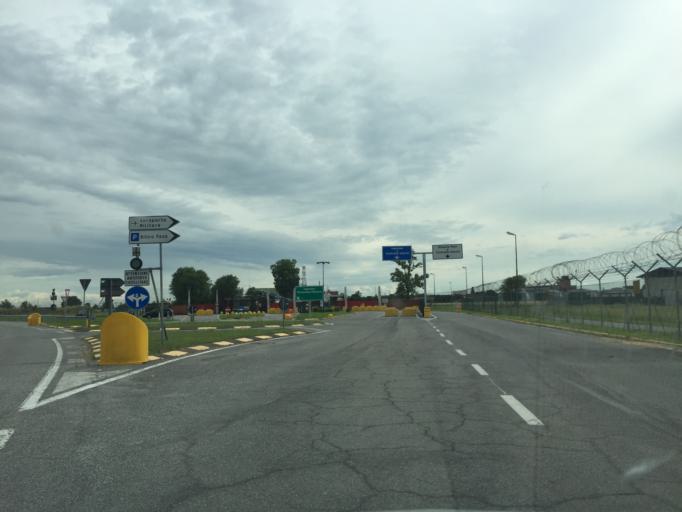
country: IT
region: Lombardy
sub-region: Provincia di Brescia
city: Ghedi
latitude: 45.4372
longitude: 10.2842
